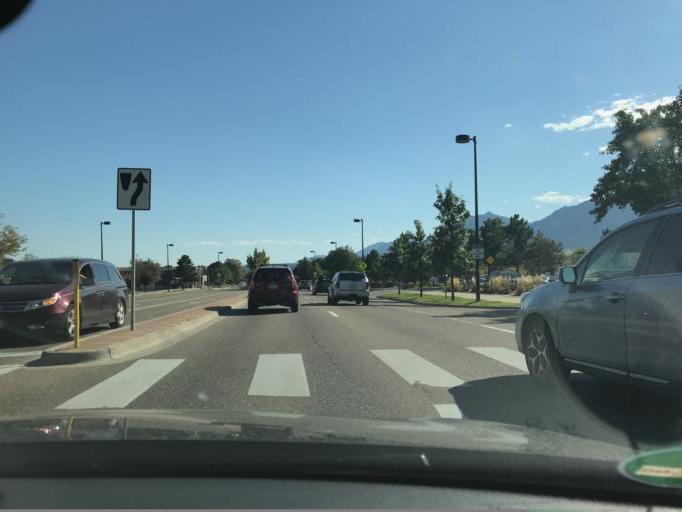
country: US
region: Colorado
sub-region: Boulder County
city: Boulder
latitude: 40.0365
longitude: -105.2585
